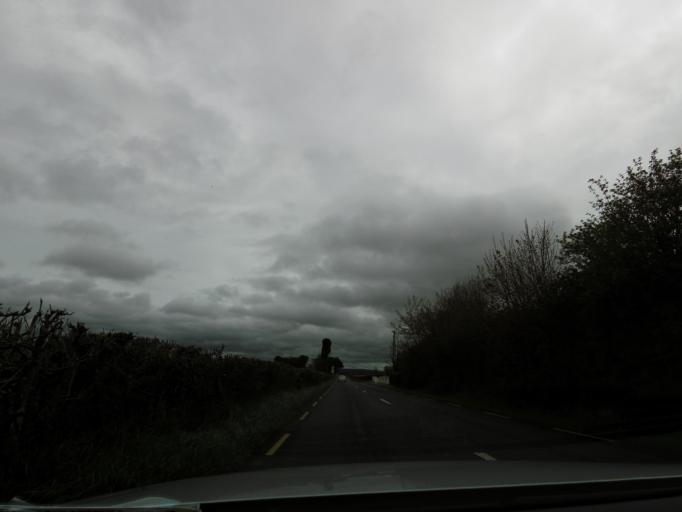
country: IE
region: Leinster
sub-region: Kilkenny
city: Ballyragget
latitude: 52.7232
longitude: -7.3543
